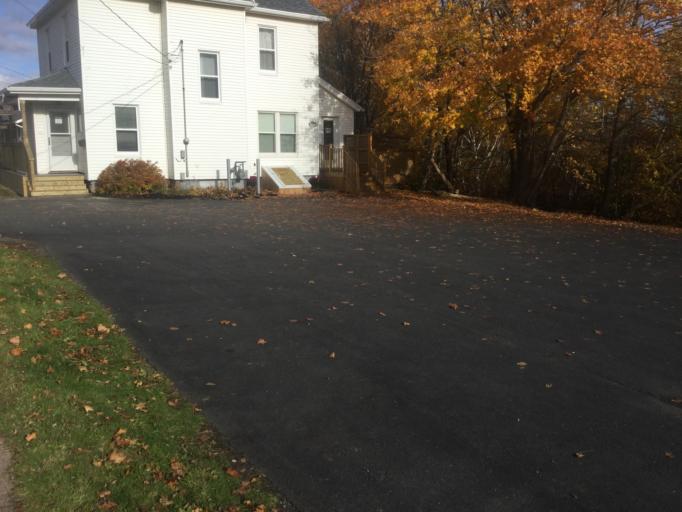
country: CA
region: Nova Scotia
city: New Glasgow
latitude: 45.5829
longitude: -62.6542
